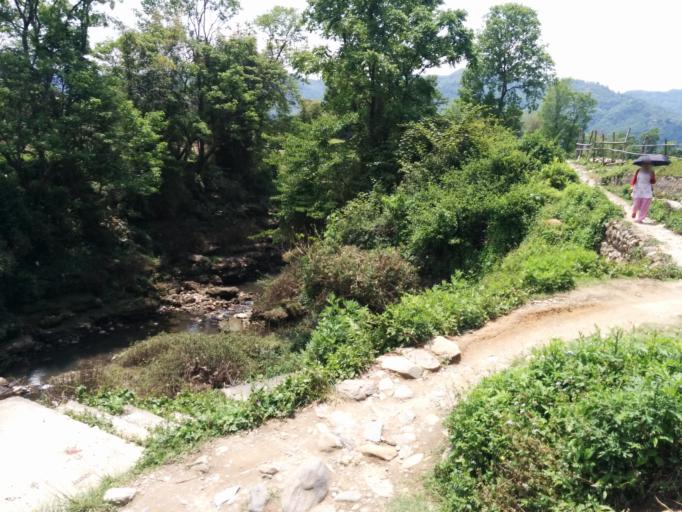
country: NP
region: Western Region
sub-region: Gandaki Zone
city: Pokhara
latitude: 28.1941
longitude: 83.9675
